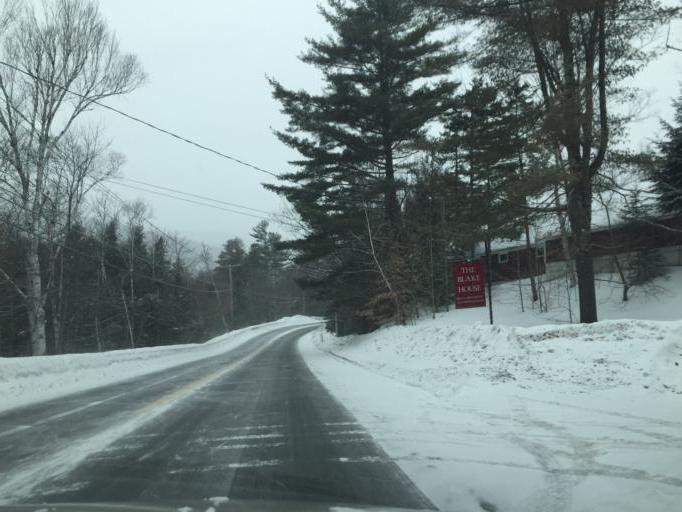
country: US
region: New Hampshire
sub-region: Carroll County
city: North Conway
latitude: 44.1912
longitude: -71.2281
